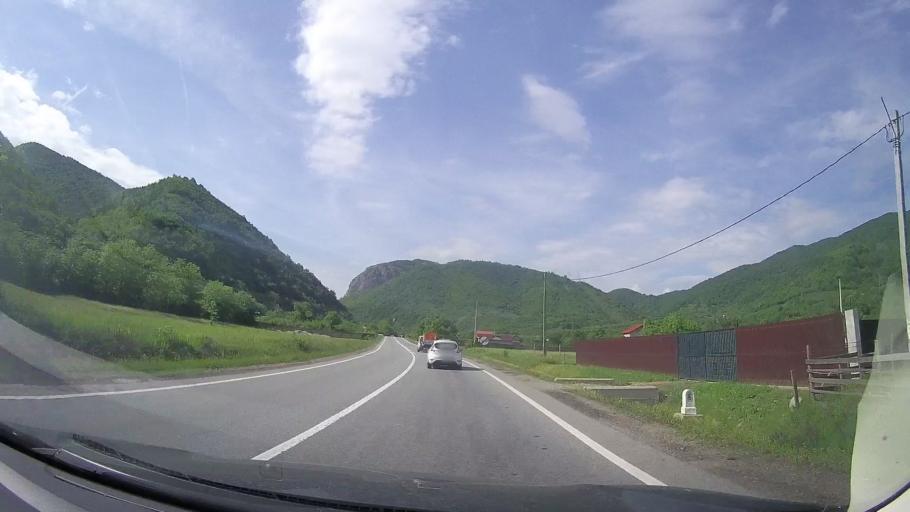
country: RO
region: Caras-Severin
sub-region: Comuna Mehadia
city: Mehadia
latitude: 44.8830
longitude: 22.3833
